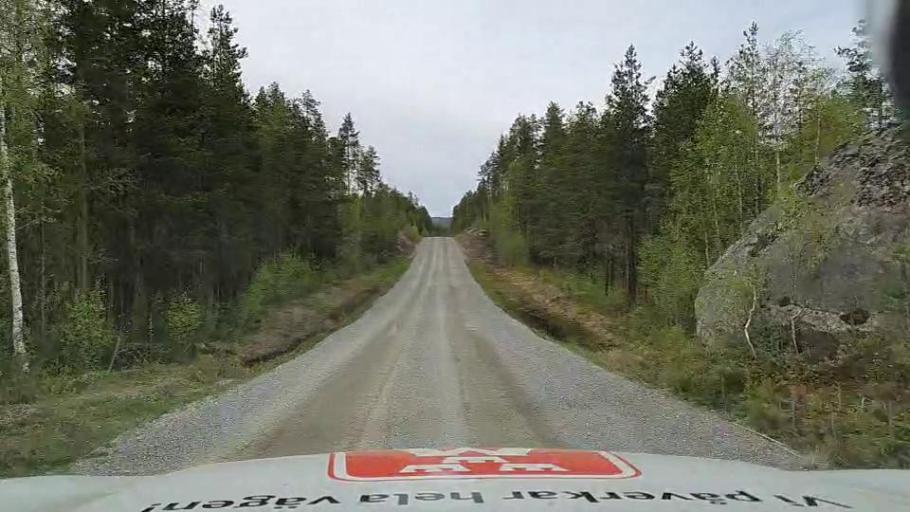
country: SE
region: Jaemtland
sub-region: Braecke Kommun
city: Braecke
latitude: 62.4750
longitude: 14.9166
